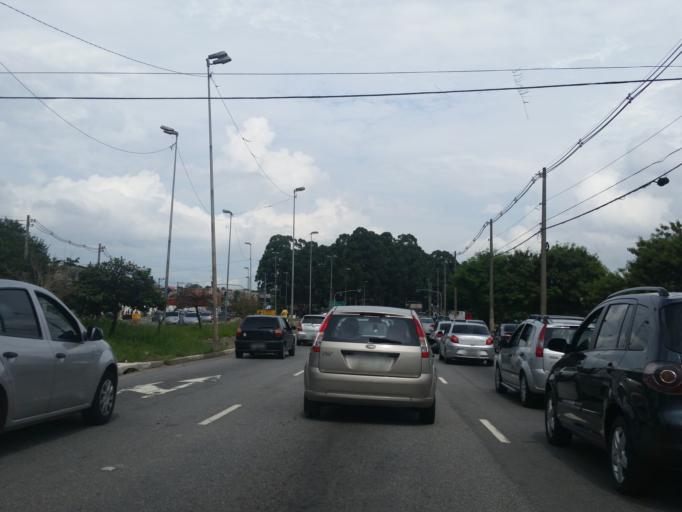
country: BR
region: Sao Paulo
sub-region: Guarulhos
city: Guarulhos
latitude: -23.5046
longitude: -46.4579
